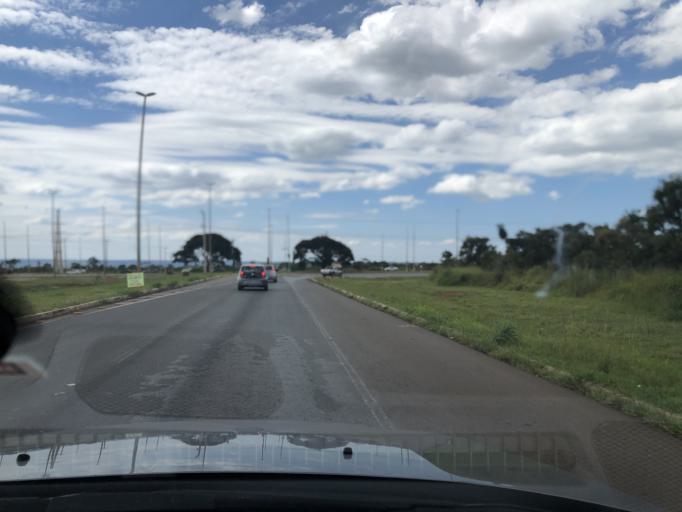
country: BR
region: Federal District
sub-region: Brasilia
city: Brasilia
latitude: -15.9771
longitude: -47.9915
